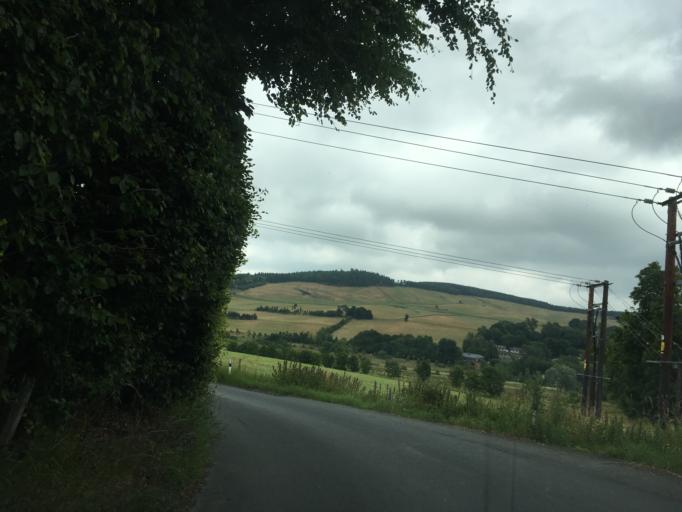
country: GB
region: Scotland
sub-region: The Scottish Borders
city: Peebles
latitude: 55.6623
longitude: -3.2019
